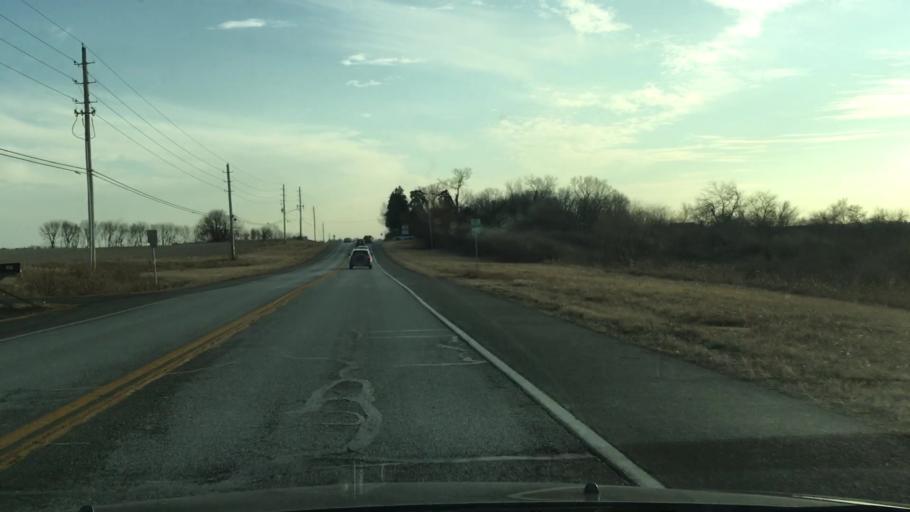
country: US
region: Missouri
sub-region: Jackson County
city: Lees Summit
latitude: 38.8832
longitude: -94.4155
